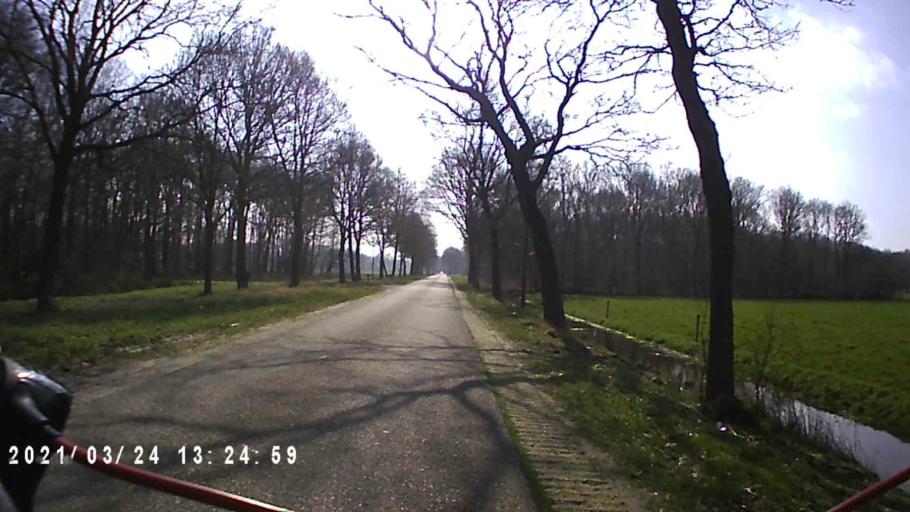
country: NL
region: Groningen
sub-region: Gemeente Grootegast
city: Grootegast
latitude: 53.0948
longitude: 6.2780
